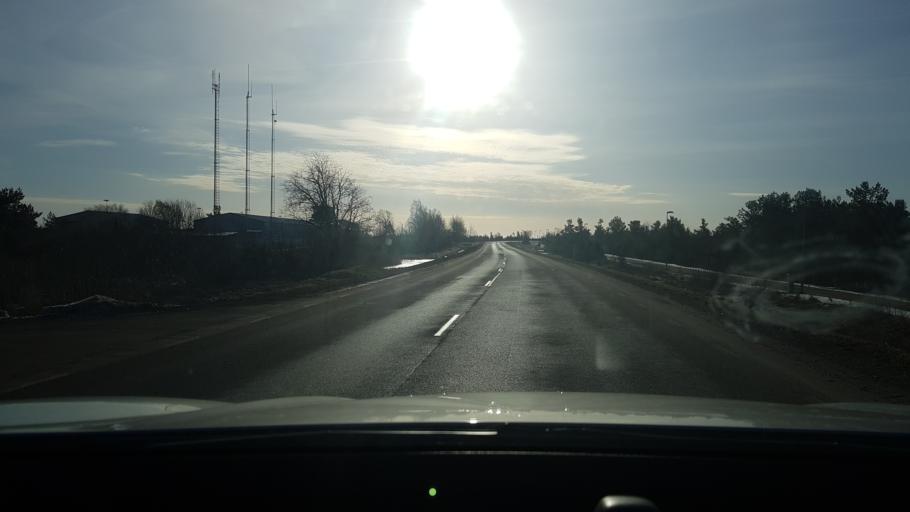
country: EE
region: Saare
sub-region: Kuressaare linn
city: Kuressaare
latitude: 58.2341
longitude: 22.5014
